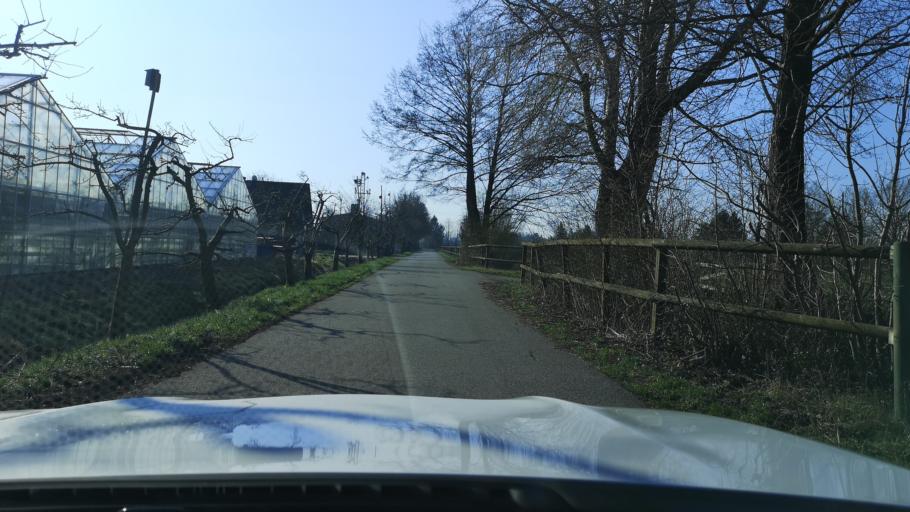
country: DE
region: Bavaria
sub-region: Upper Bavaria
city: Eichenried
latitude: 48.2370
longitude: 11.7703
